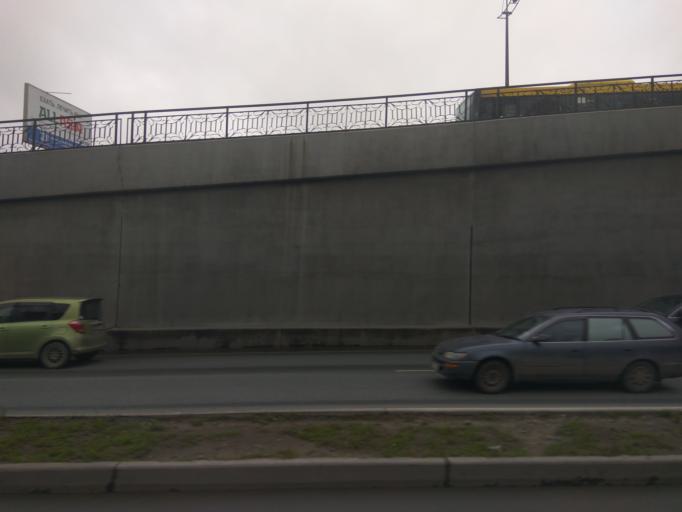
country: RU
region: Primorskiy
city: Vladivostok
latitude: 43.1189
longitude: 131.9013
